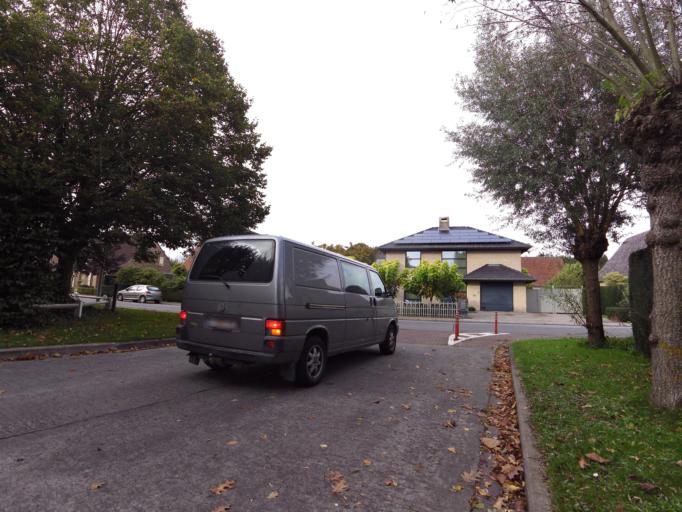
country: BE
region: Flanders
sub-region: Provincie West-Vlaanderen
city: Sint-Kruis
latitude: 51.1911
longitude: 3.2480
